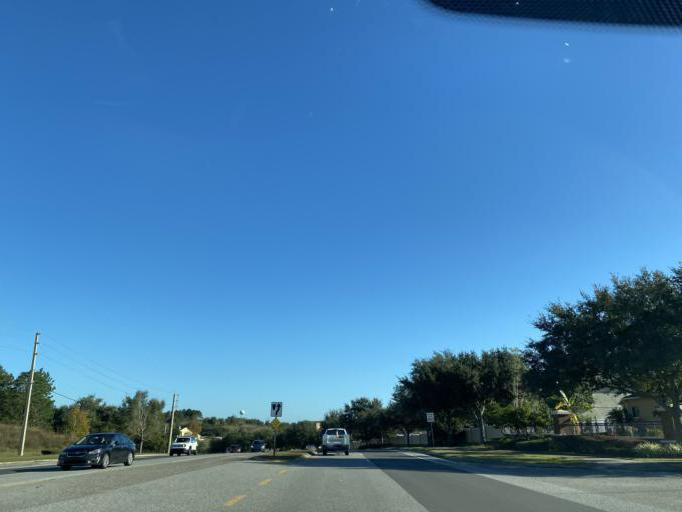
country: US
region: Florida
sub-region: Lake County
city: Minneola
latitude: 28.5345
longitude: -81.7248
